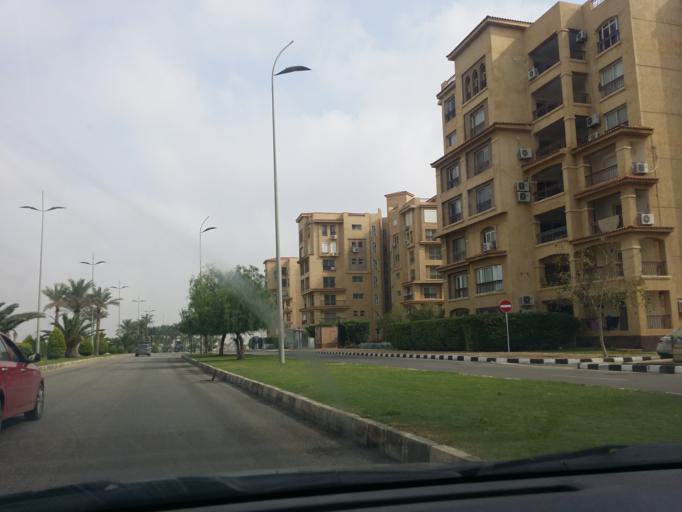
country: EG
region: Muhafazat al Qalyubiyah
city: Al Khankah
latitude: 30.1033
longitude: 31.6325
